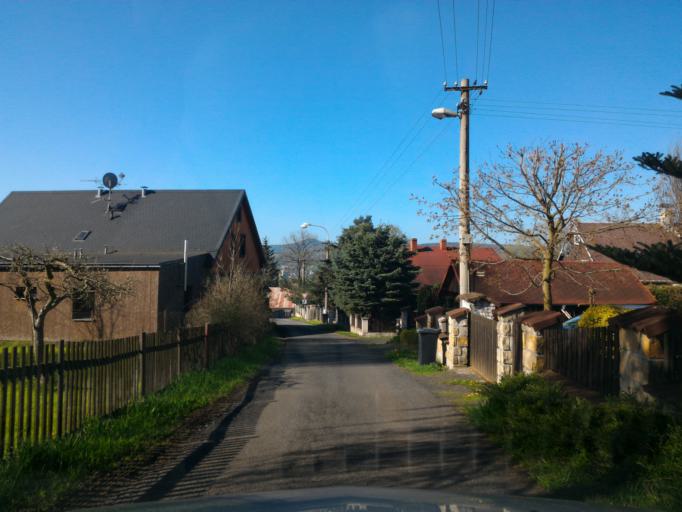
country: CZ
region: Ustecky
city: Varnsdorf
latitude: 50.9179
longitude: 14.6366
